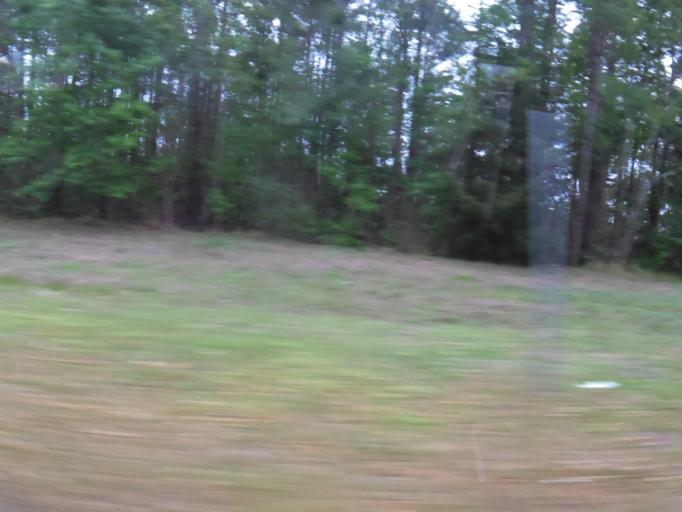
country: US
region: Florida
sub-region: Nassau County
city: Nassau Village-Ratliff
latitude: 30.4888
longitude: -81.6788
